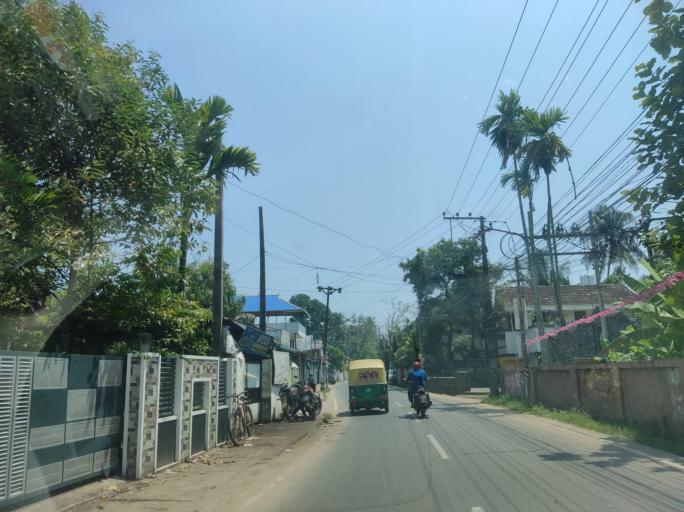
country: IN
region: Kerala
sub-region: Ernakulam
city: Cochin
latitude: 9.8906
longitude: 76.2852
